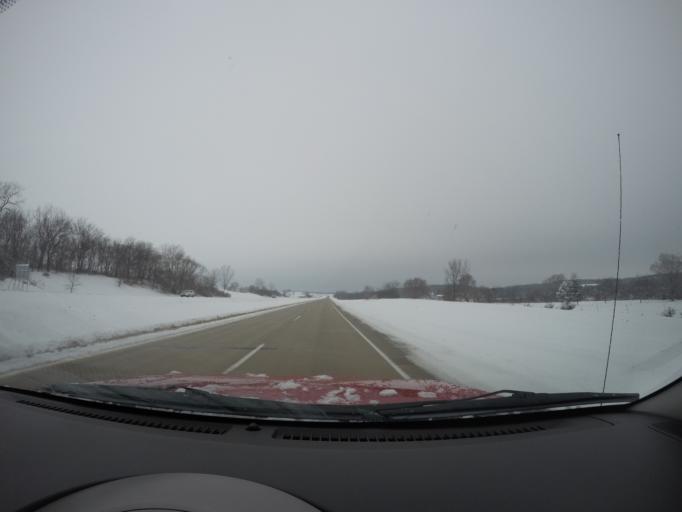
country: US
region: Minnesota
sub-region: Olmsted County
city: Rochester
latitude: 43.9624
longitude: -92.3875
